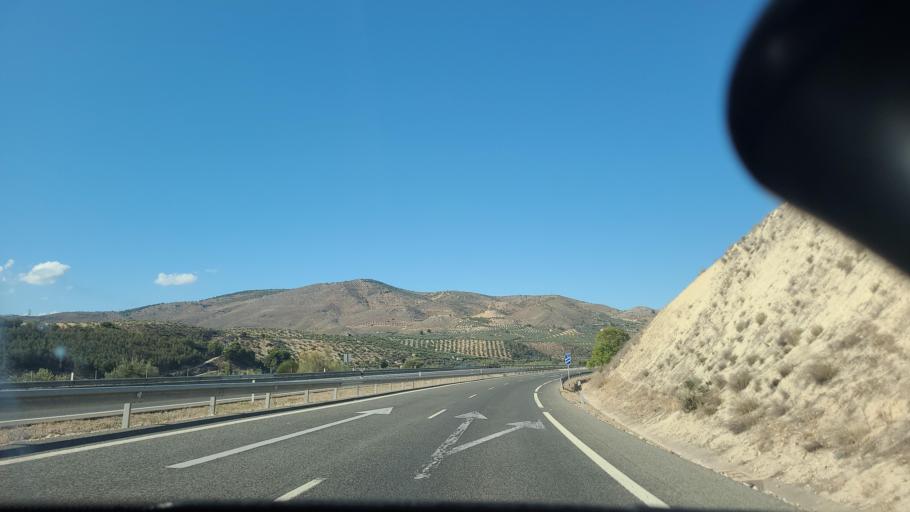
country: ES
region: Andalusia
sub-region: Provincia de Jaen
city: La Guardia de Jaen
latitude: 37.7182
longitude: -3.6740
